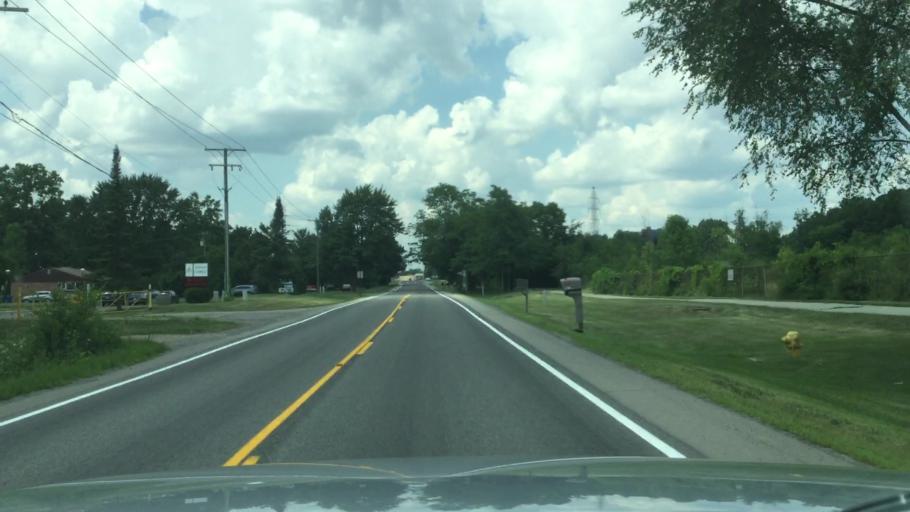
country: US
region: Michigan
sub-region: Washtenaw County
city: Ypsilanti
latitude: 42.2052
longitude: -83.6121
